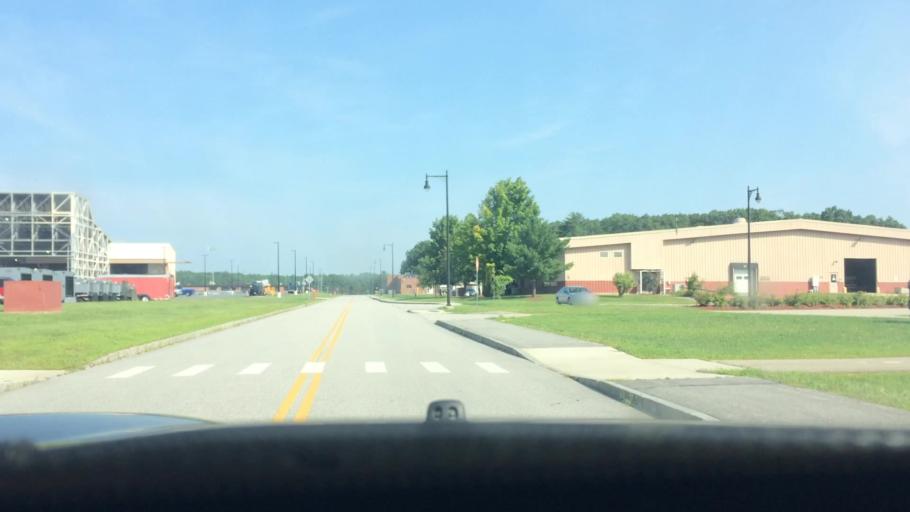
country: US
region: Maine
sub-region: York County
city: South Eliot
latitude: 43.0867
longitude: -70.8170
